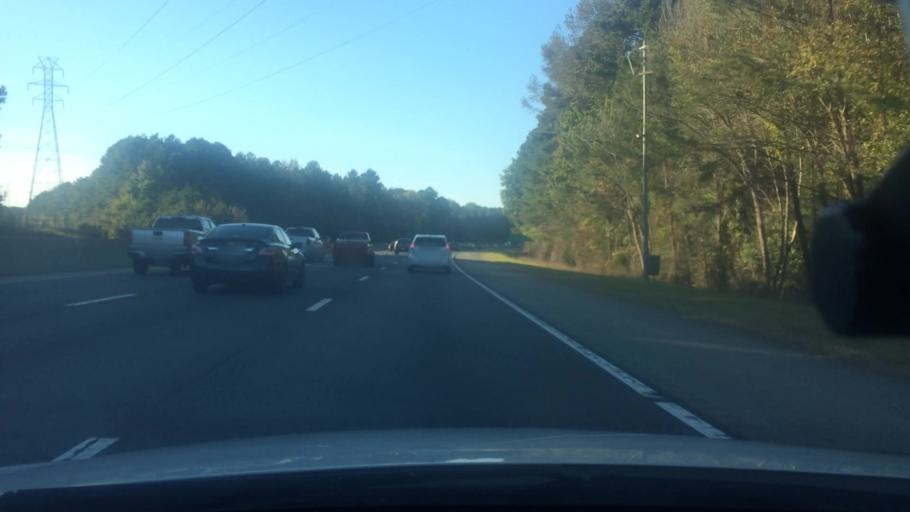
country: US
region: North Carolina
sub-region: Orange County
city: Chapel Hill
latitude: 35.9062
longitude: -78.9739
